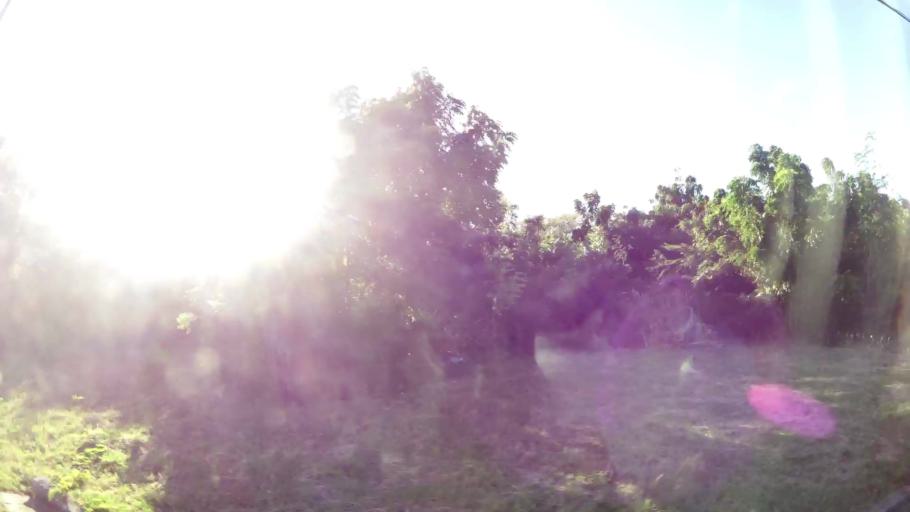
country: AG
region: Saint George
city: Piggotts
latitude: 17.1252
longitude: -61.7899
